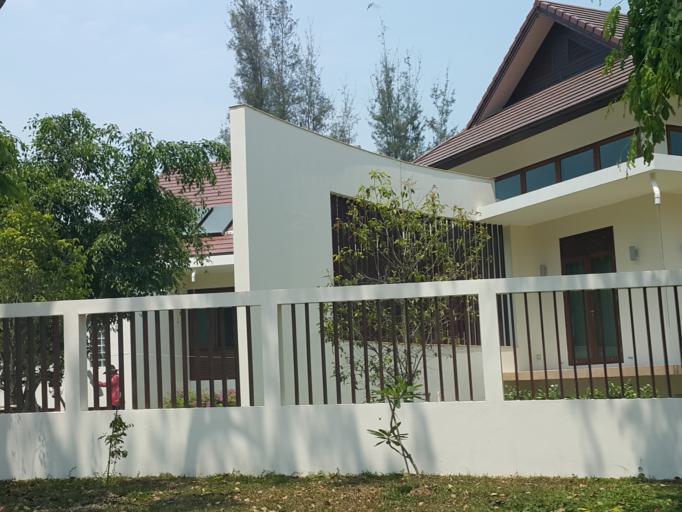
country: TH
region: Chiang Mai
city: Saraphi
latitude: 18.7271
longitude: 98.9762
